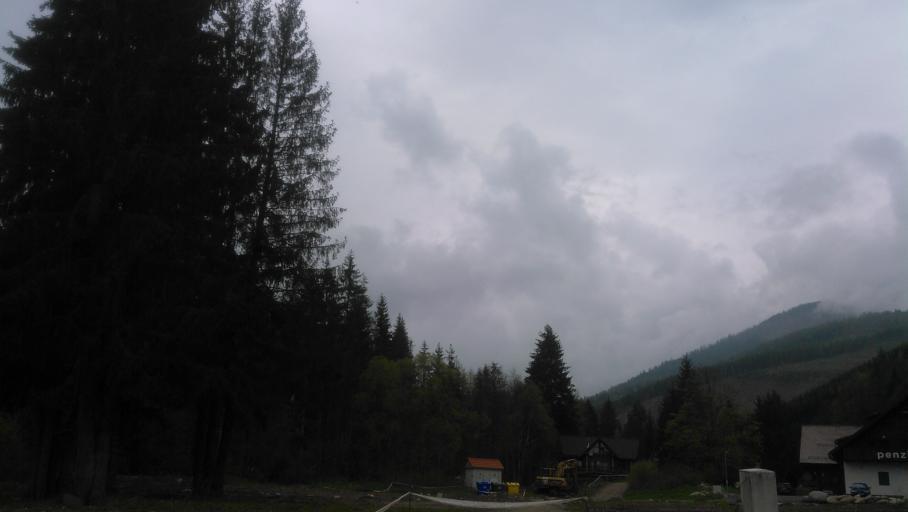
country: SK
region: Banskobystricky
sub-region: Okres Banska Bystrica
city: Brezno
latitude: 48.8647
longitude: 19.6054
